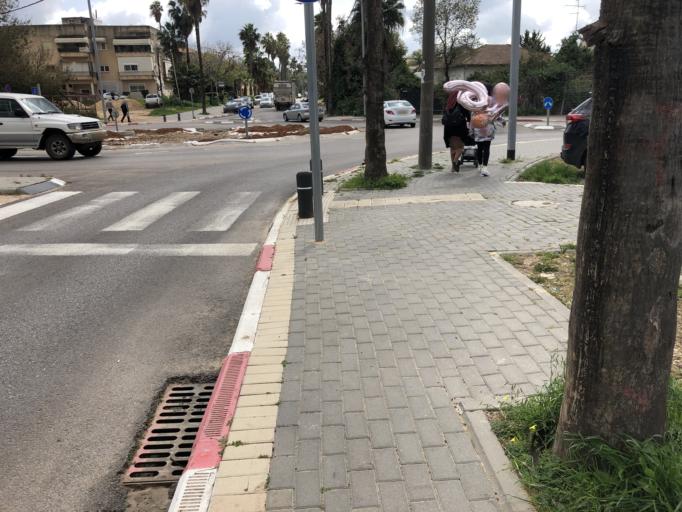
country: IL
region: Haifa
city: Hadera
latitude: 32.4729
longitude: 34.9741
